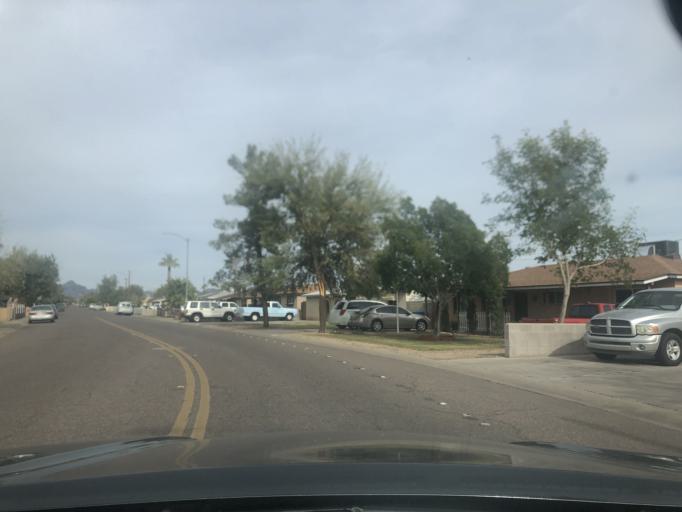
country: US
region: Arizona
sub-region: Maricopa County
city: Phoenix
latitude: 33.4531
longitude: -112.0211
